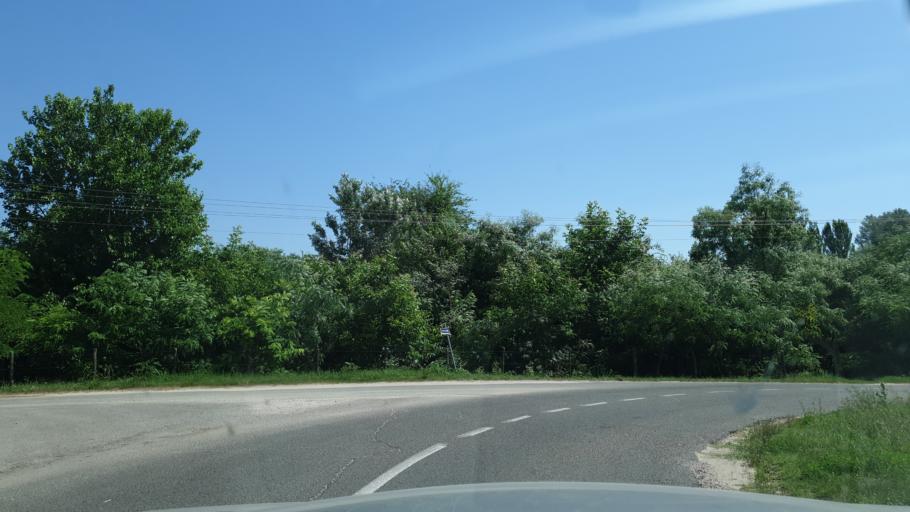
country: HU
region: Csongrad
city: Morahalom
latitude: 46.1268
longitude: 19.8529
